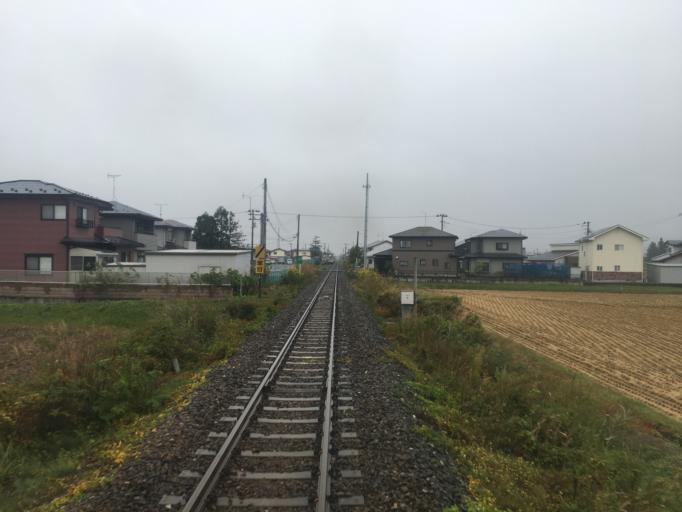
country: JP
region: Miyagi
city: Furukawa
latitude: 38.5727
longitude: 140.9338
